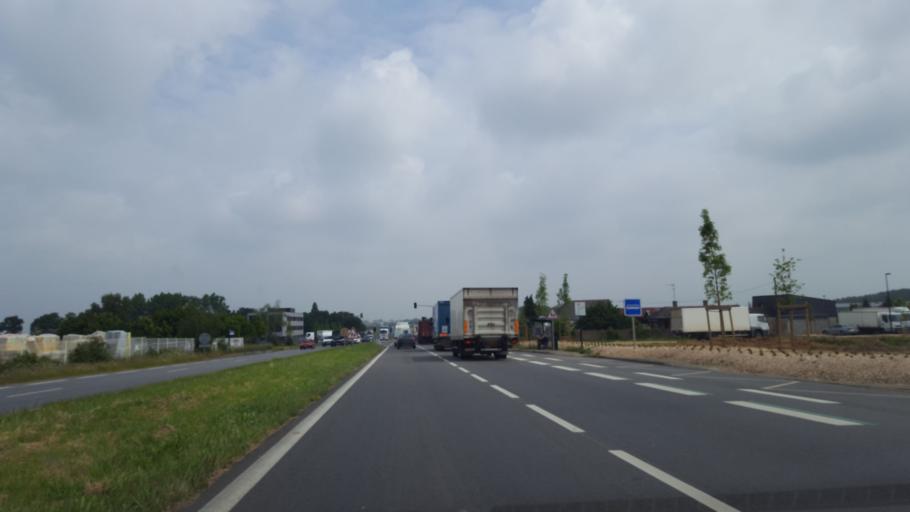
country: FR
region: Brittany
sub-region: Departement d'Ille-et-Vilaine
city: Saint-Jacques-de-la-Lande
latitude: 48.0680
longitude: -1.6979
